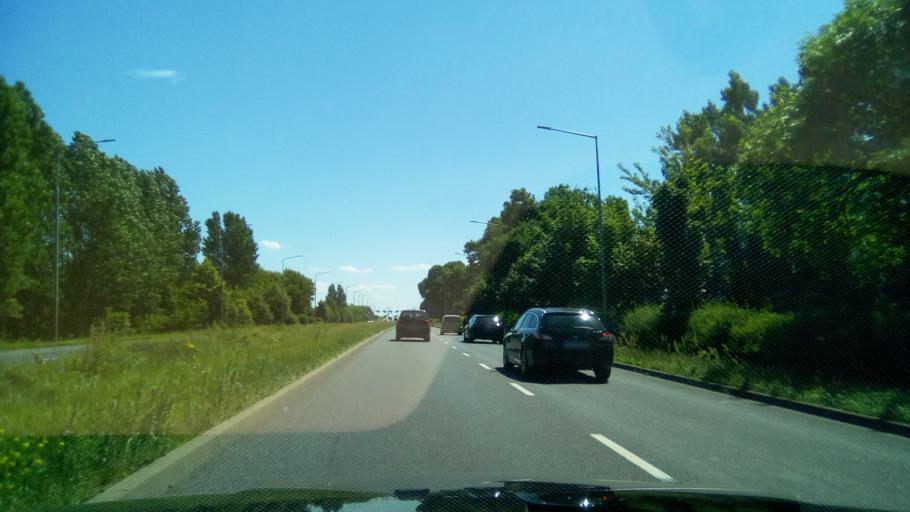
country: PL
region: Masovian Voivodeship
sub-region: Radom
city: Radom
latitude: 51.4223
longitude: 21.1742
